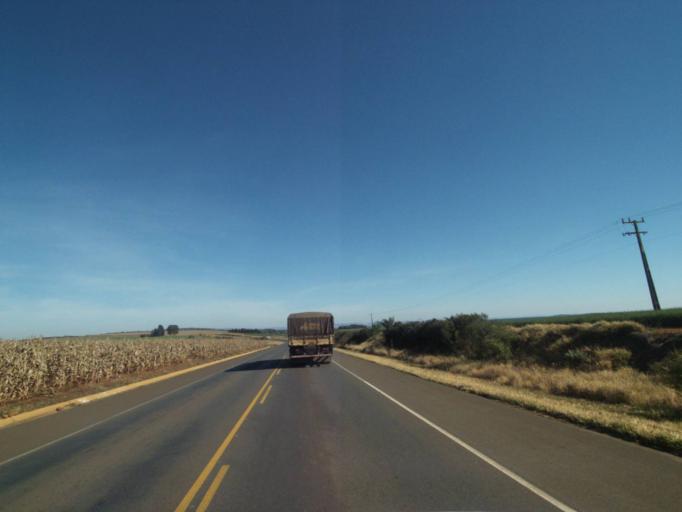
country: BR
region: Parana
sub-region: Tibagi
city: Tibagi
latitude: -24.3797
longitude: -50.3289
